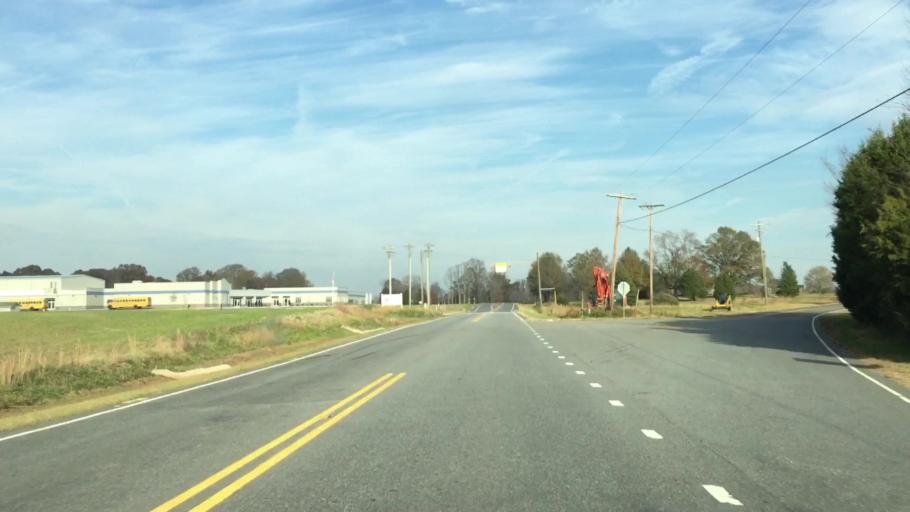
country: US
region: North Carolina
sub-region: Guilford County
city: Summerfield
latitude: 36.2599
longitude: -79.8711
